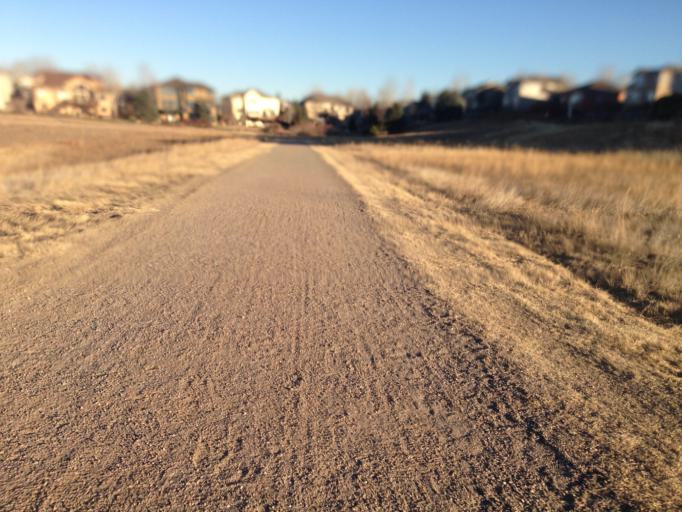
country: US
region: Colorado
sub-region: Broomfield County
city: Broomfield
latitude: 39.9367
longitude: -105.0878
